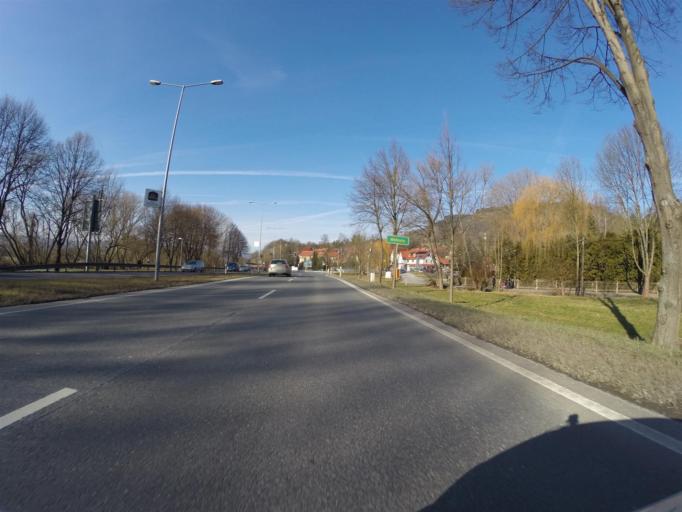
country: DE
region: Thuringia
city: Jena
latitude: 50.9019
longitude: 11.5986
